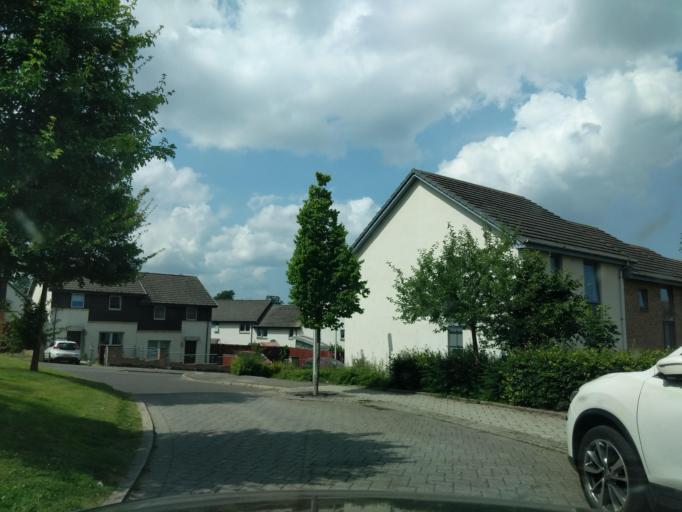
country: GB
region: Scotland
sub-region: Midlothian
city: Loanhead
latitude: 55.9058
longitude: -3.1568
